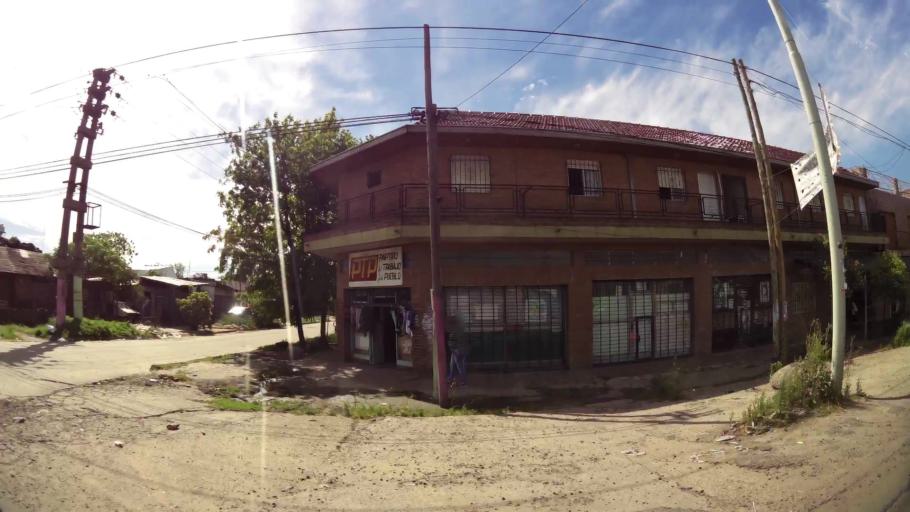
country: AR
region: Buenos Aires
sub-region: Partido de Almirante Brown
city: Adrogue
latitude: -34.7893
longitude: -58.3084
